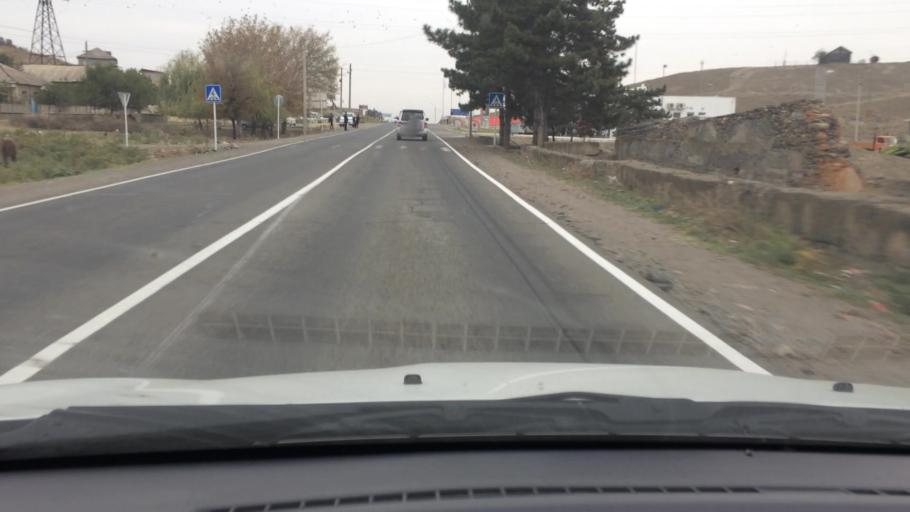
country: GE
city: Naghvarevi
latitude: 41.3624
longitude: 44.8363
